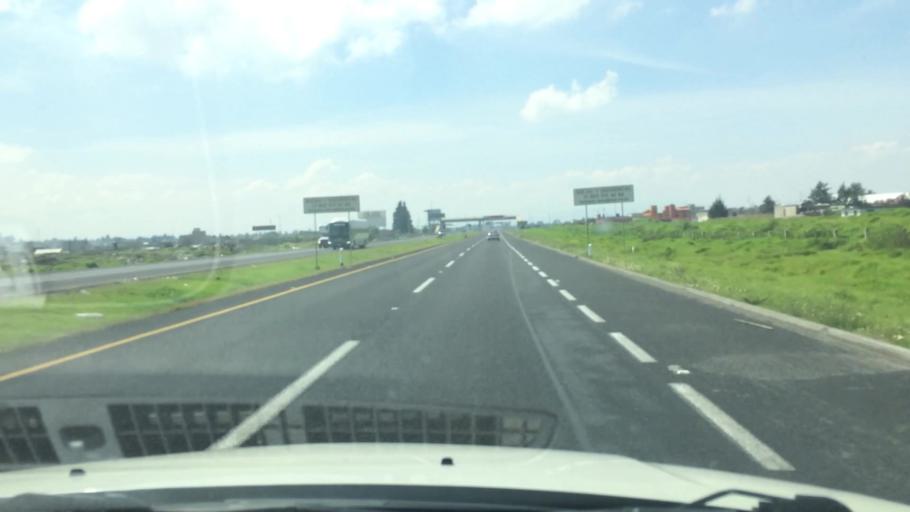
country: MX
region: Mexico
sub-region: Lerma
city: Colonia Isidro Fabela
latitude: 19.3030
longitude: -99.5212
